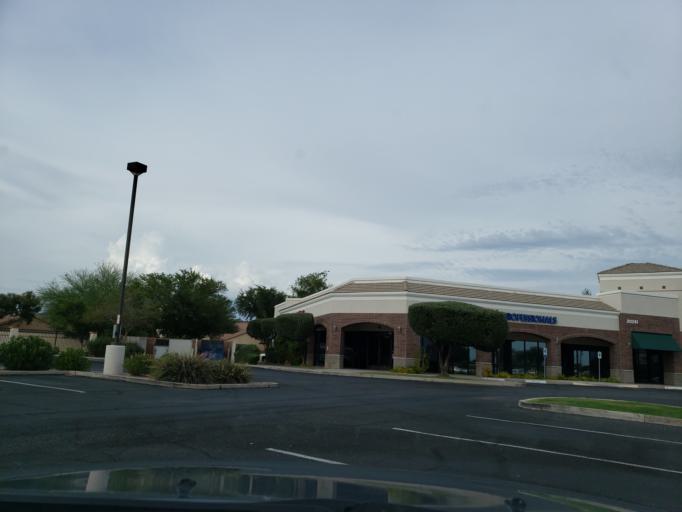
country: US
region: Arizona
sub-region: Maricopa County
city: Peoria
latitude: 33.6710
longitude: -112.2014
